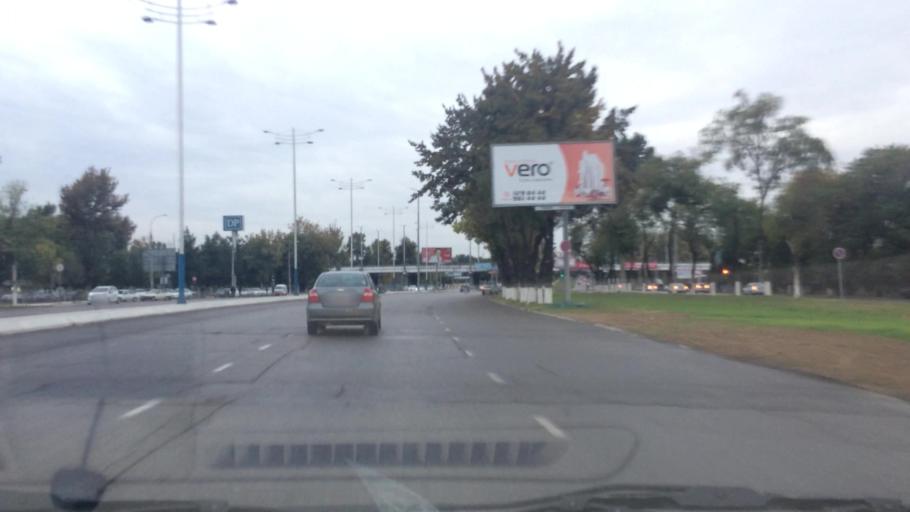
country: UZ
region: Toshkent Shahri
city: Tashkent
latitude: 41.2578
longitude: 69.1948
